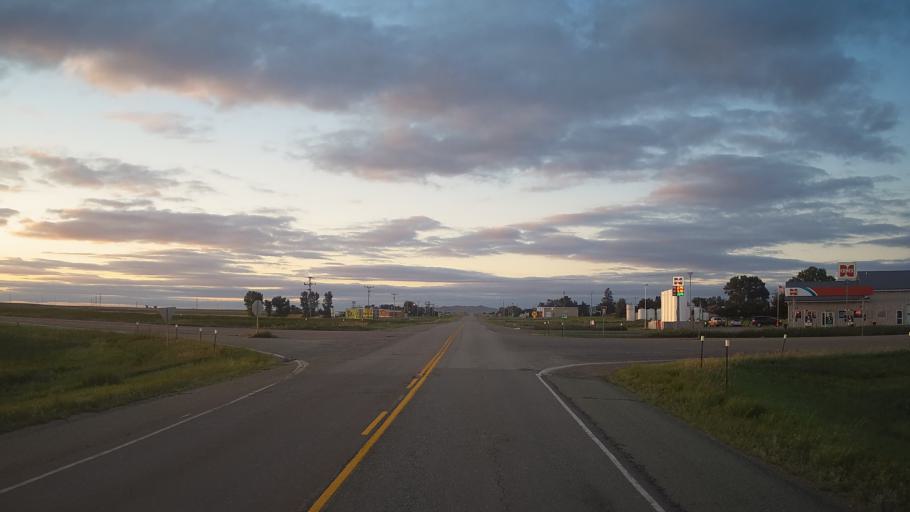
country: US
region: South Dakota
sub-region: Buffalo County
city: Fort Thompson
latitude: 43.8747
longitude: -99.6059
